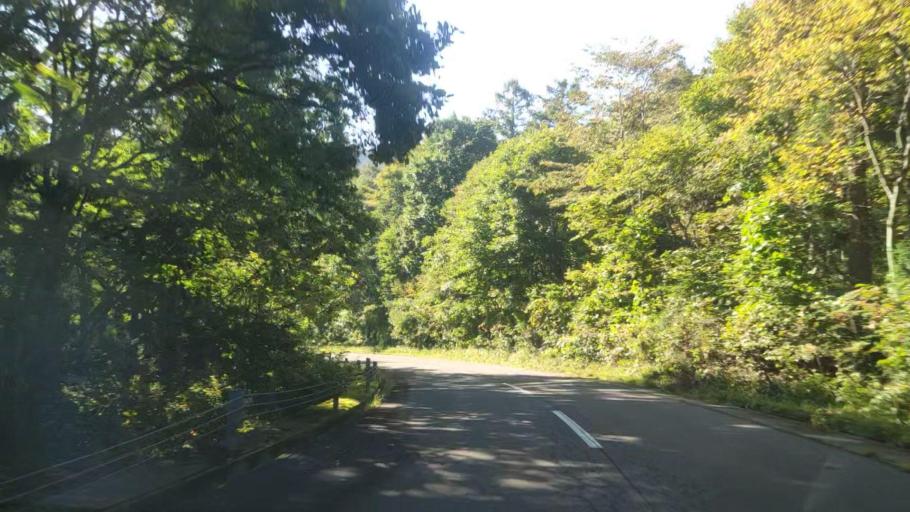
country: JP
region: Nagano
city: Iiyama
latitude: 36.8108
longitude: 138.4126
